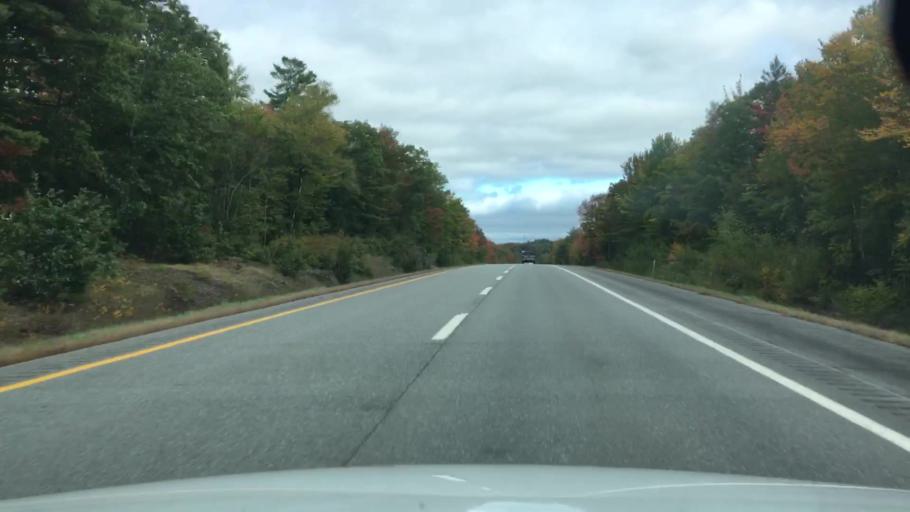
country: US
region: Maine
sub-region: Penobscot County
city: Carmel
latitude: 44.7778
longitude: -69.0593
